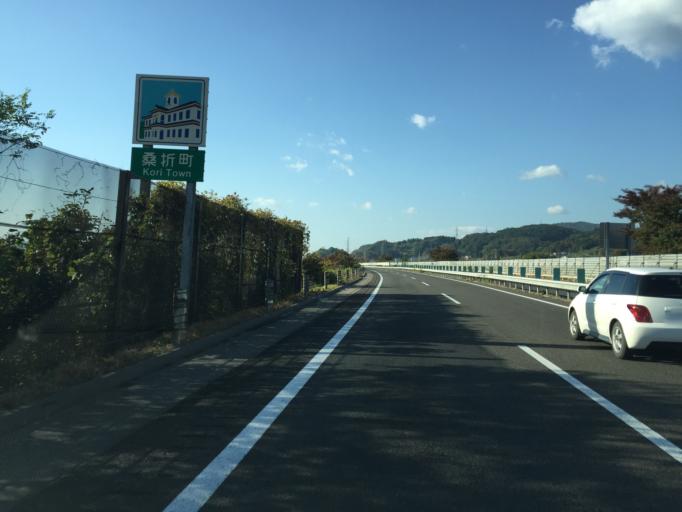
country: JP
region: Fukushima
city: Hobaramachi
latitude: 37.8762
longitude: 140.5256
